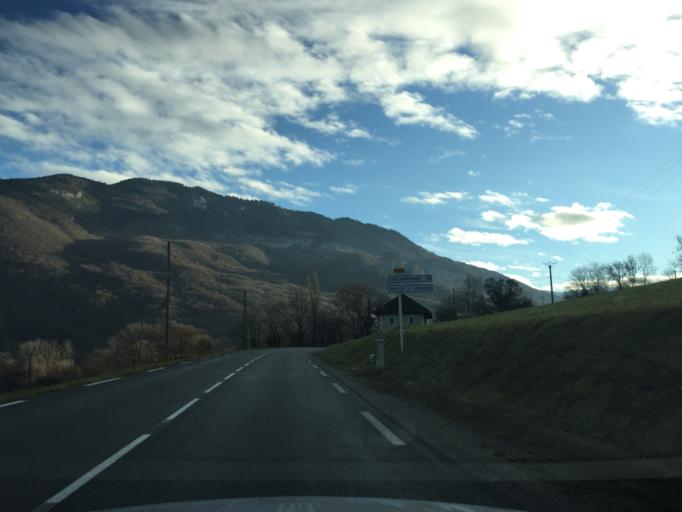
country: FR
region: Rhone-Alpes
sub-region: Departement de la Haute-Savoie
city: Cusy
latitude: 45.7640
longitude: 6.0457
